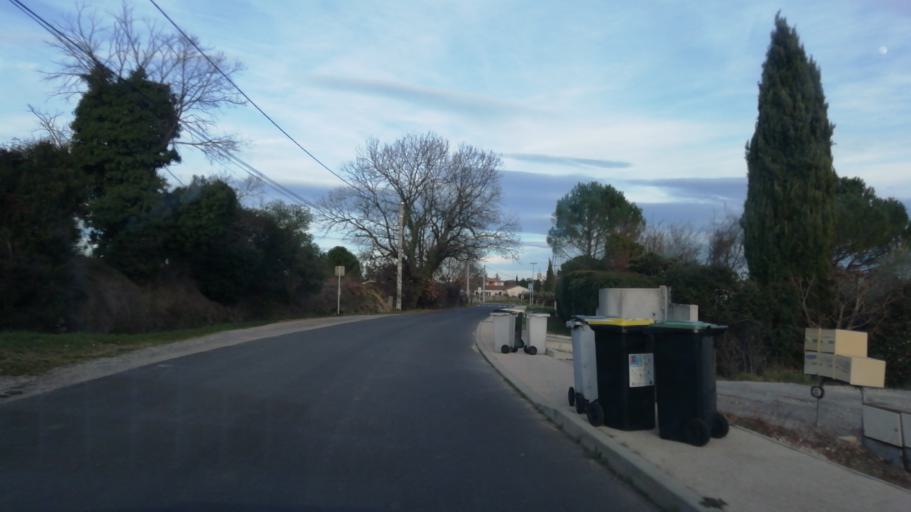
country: FR
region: Languedoc-Roussillon
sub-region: Departement de l'Herault
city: Claret
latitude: 43.8416
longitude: 3.9376
